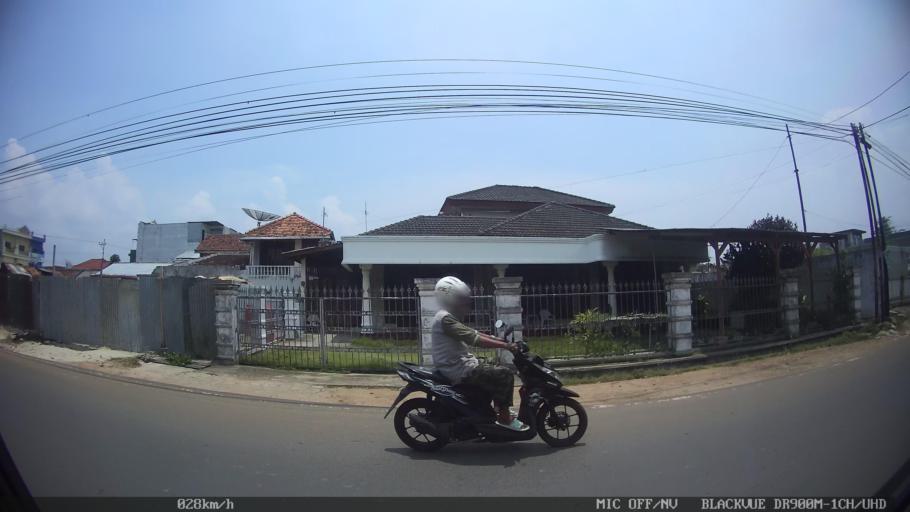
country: ID
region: Lampung
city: Bandarlampung
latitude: -5.4419
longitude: 105.2734
